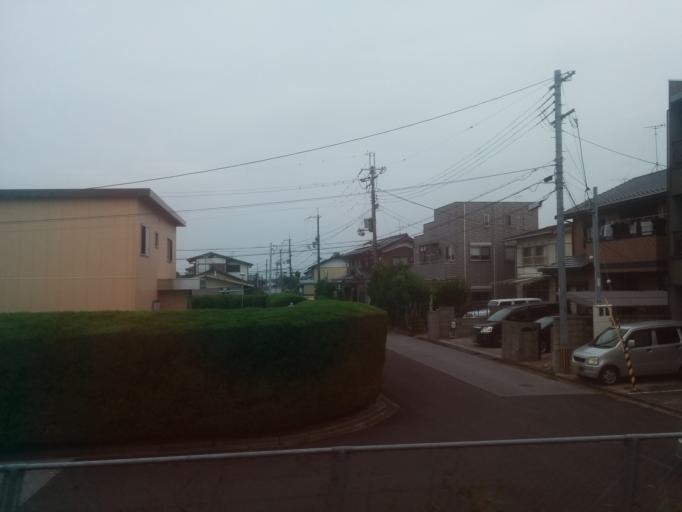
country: JP
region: Shiga Prefecture
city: Hikone
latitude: 35.2481
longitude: 136.2502
